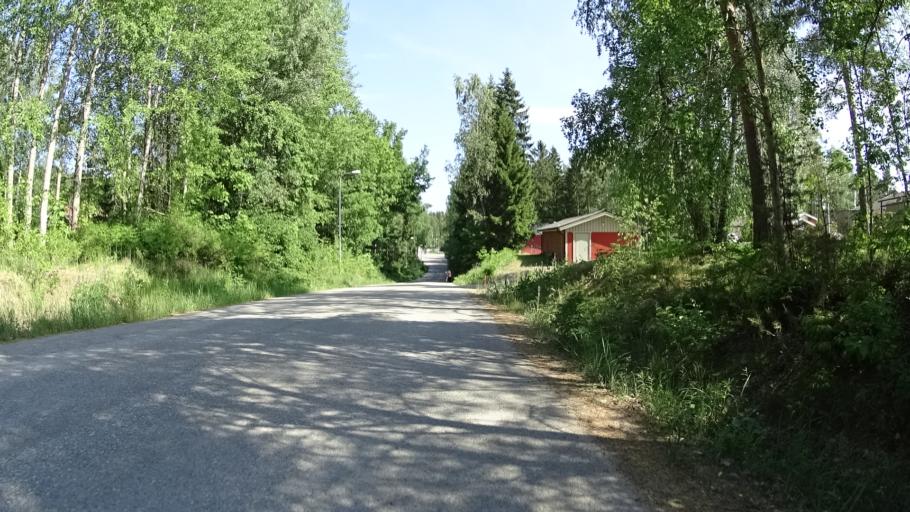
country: FI
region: Uusimaa
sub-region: Raaseporin
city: Karis
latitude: 60.0829
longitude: 23.6575
